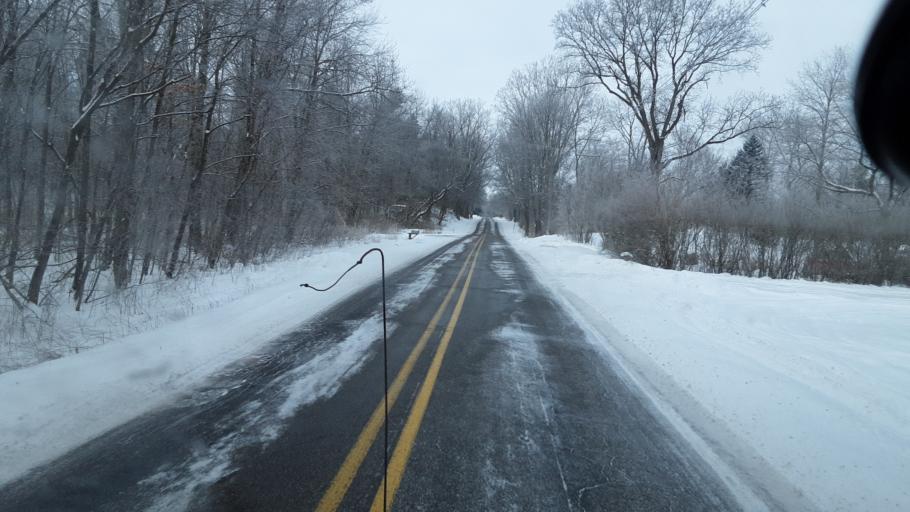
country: US
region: Michigan
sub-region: Eaton County
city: Eaton Rapids
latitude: 42.4656
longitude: -84.5498
